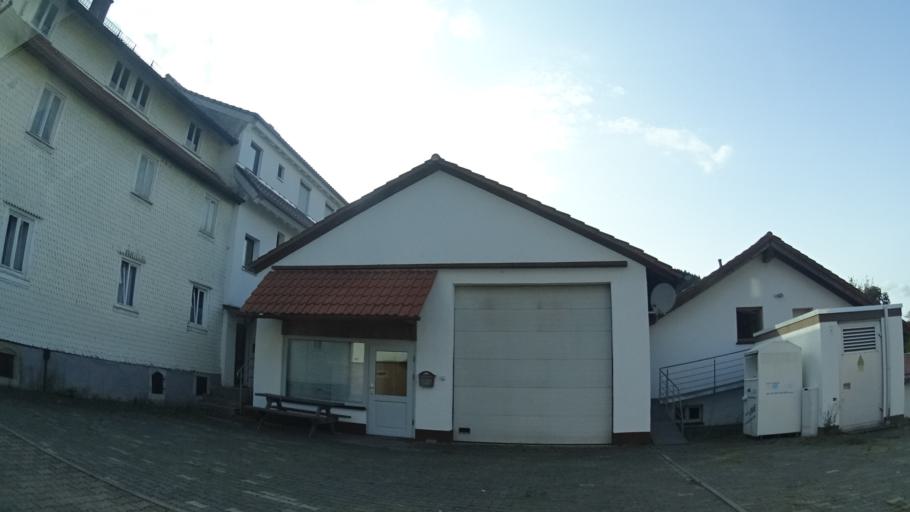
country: DE
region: Baden-Wuerttemberg
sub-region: Karlsruhe Region
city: Heddesbach
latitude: 49.5232
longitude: 8.8629
